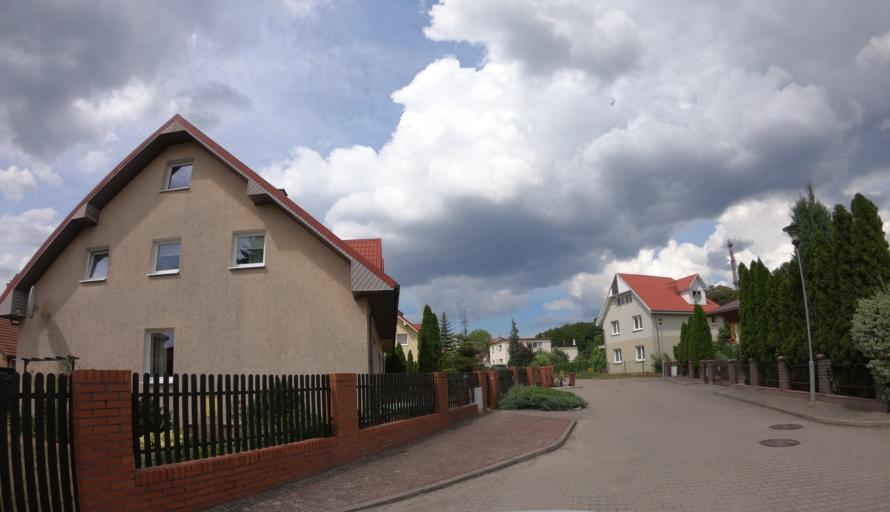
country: PL
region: West Pomeranian Voivodeship
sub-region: Powiat gryfinski
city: Stare Czarnowo
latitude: 53.3568
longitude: 14.7493
